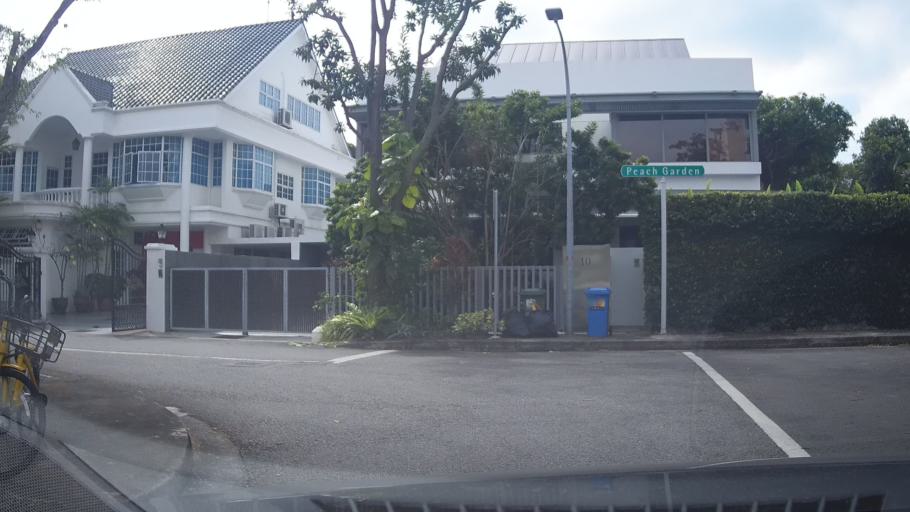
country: SG
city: Singapore
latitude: 1.2976
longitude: 103.8960
